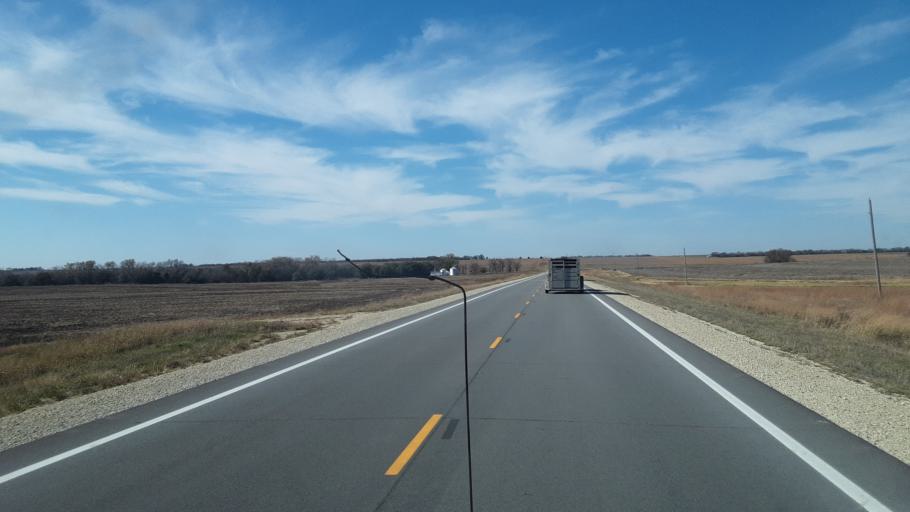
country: US
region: Kansas
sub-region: Marion County
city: Marion
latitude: 38.3630
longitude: -96.8649
